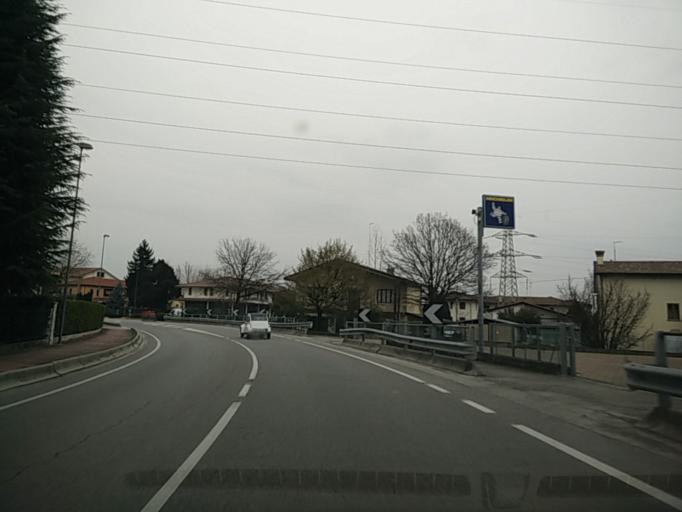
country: IT
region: Veneto
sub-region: Provincia di Venezia
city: Scorze
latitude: 45.5680
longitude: 12.1074
